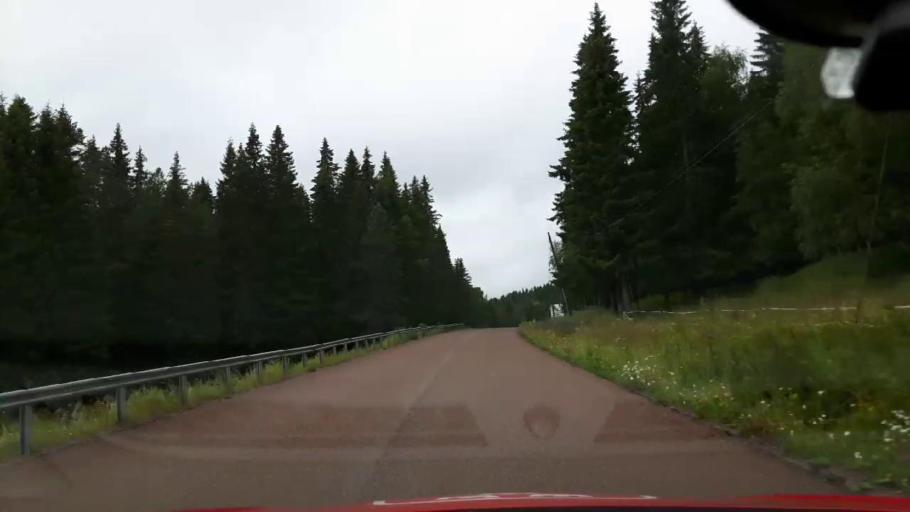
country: SE
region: Jaemtland
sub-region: Krokoms Kommun
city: Valla
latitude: 63.3895
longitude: 13.8629
